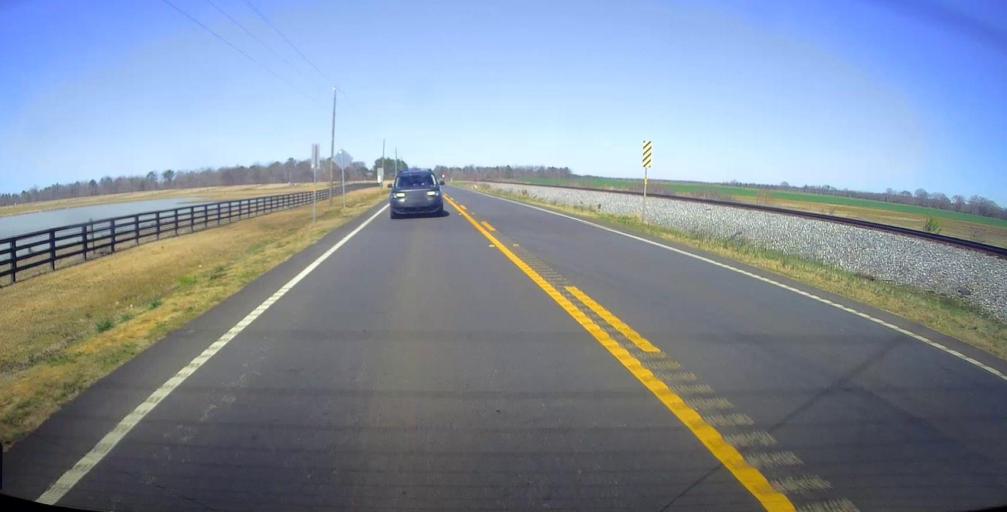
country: US
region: Georgia
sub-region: Macon County
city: Marshallville
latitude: 32.4681
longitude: -83.9367
